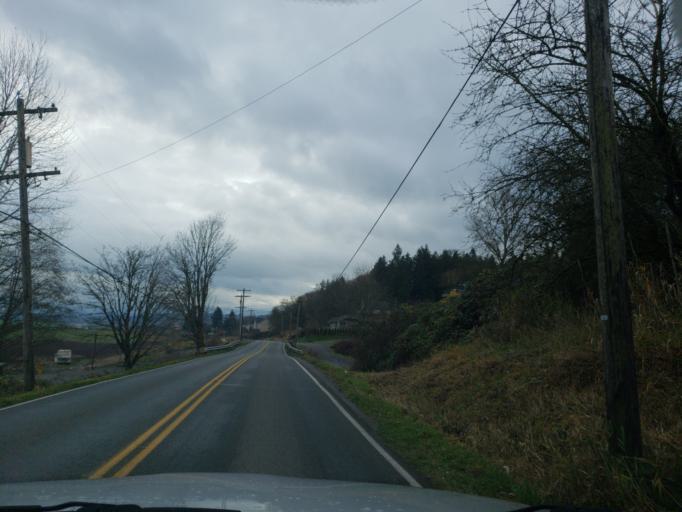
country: US
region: Washington
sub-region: Snohomish County
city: Silver Firs
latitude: 47.8946
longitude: -122.1525
